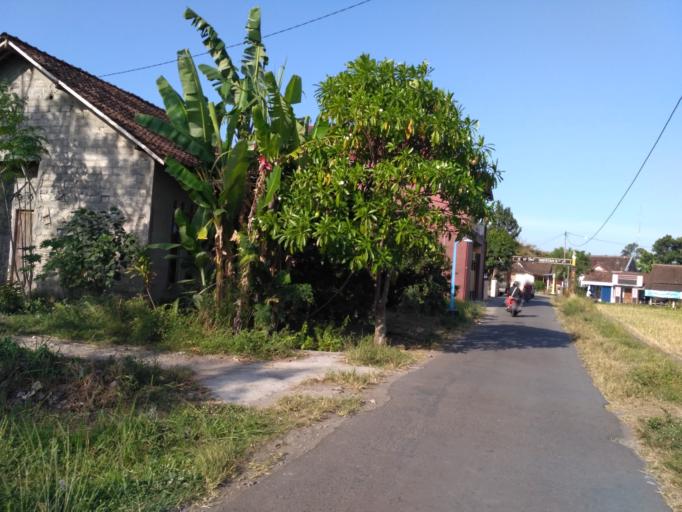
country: ID
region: Daerah Istimewa Yogyakarta
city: Depok
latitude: -7.7741
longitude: 110.4265
